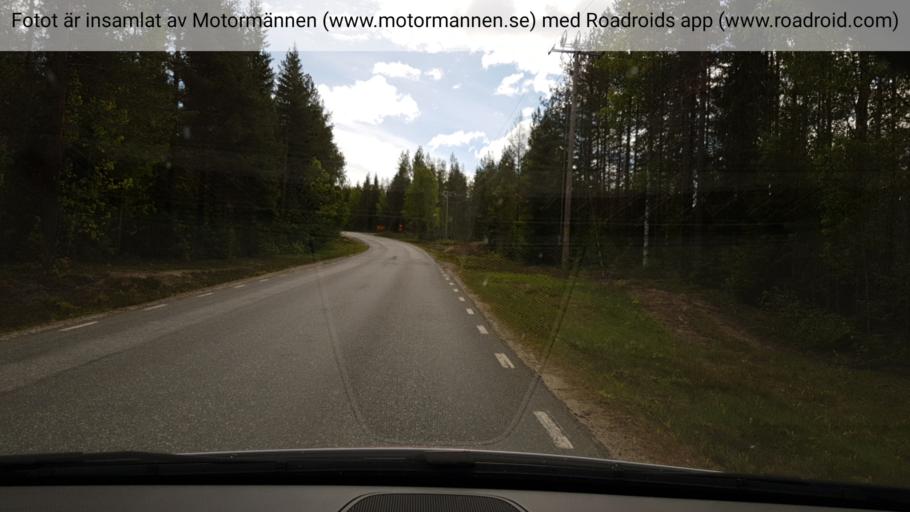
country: SE
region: Vaesterbotten
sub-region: Vannas Kommun
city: Vannasby
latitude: 64.0676
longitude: 19.9880
